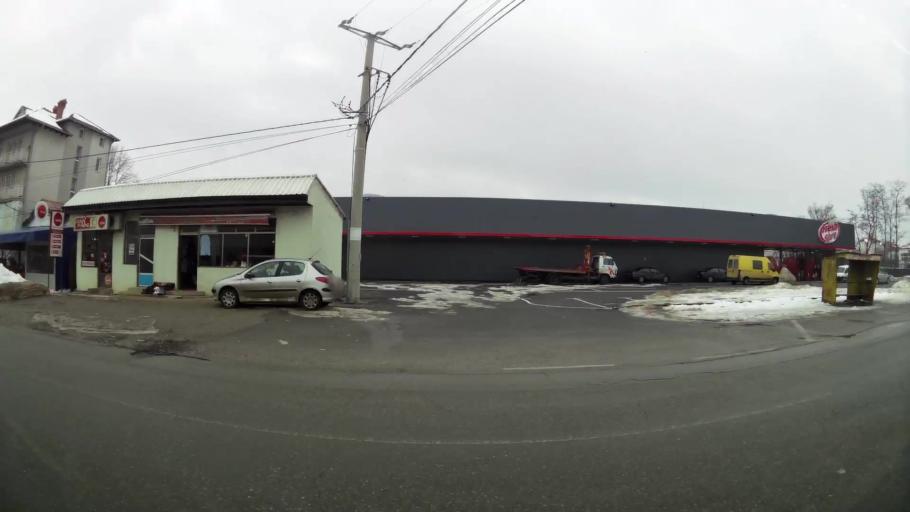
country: XK
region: Pristina
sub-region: Komuna e Prishtines
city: Pristina
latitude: 42.7167
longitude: 21.1493
